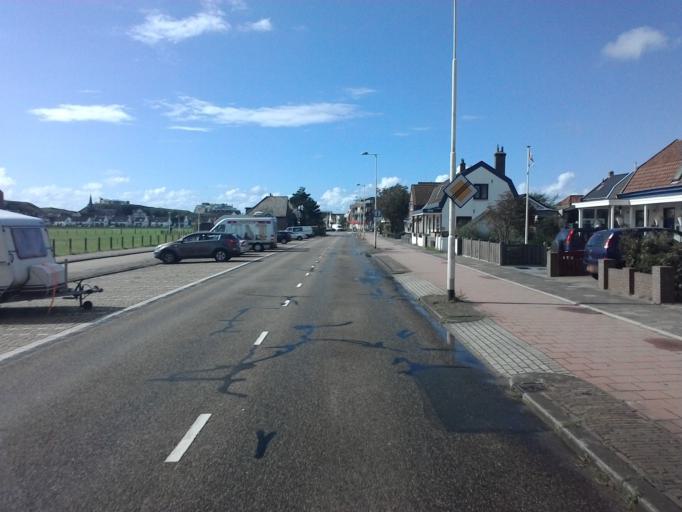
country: NL
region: North Holland
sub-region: Gemeente Beverwijk
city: Beverwijk
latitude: 52.4928
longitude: 4.6003
